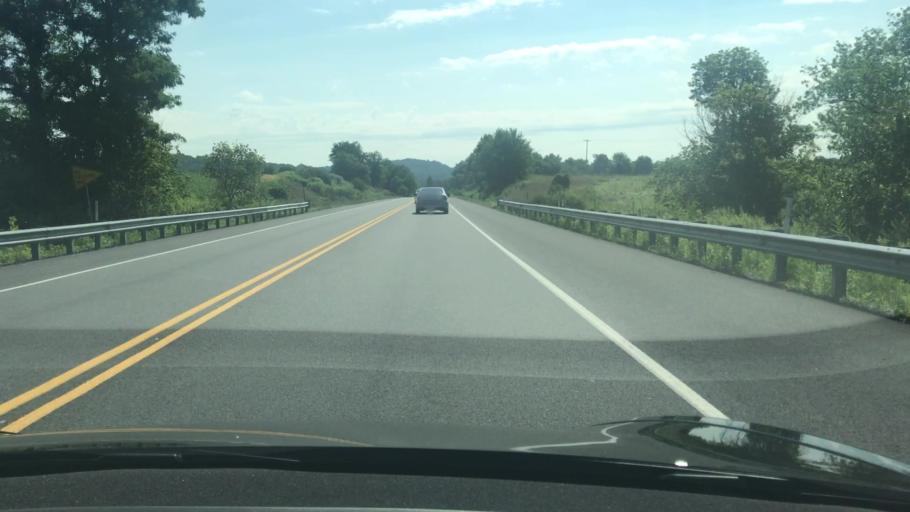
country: US
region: Pennsylvania
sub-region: York County
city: Valley Green
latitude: 40.1309
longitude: -76.8406
